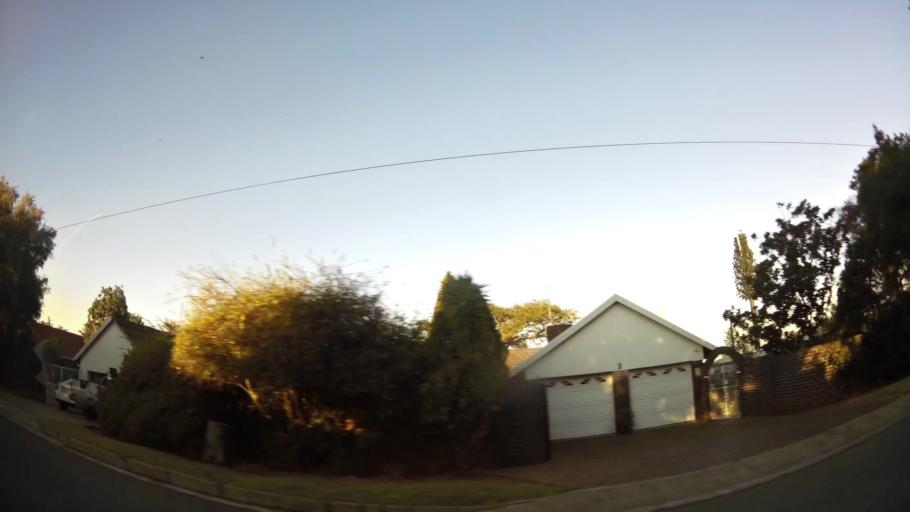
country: ZA
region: Gauteng
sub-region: City of Johannesburg Metropolitan Municipality
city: Roodepoort
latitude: -26.1551
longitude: 27.8987
